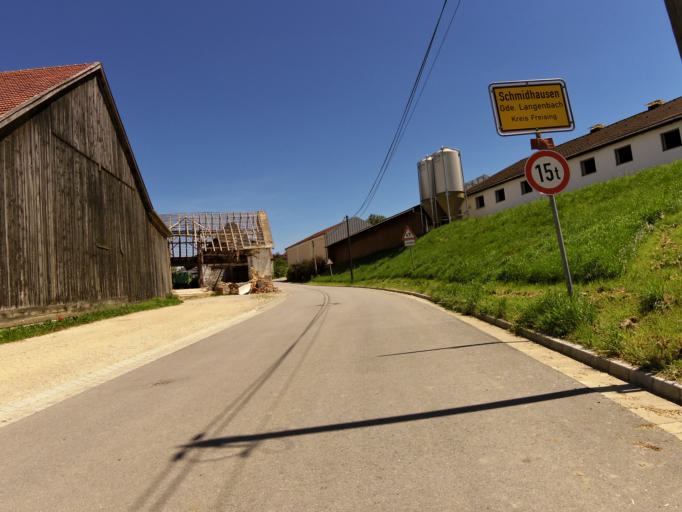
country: DE
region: Bavaria
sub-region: Upper Bavaria
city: Langenbach
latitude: 48.4231
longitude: 11.8298
